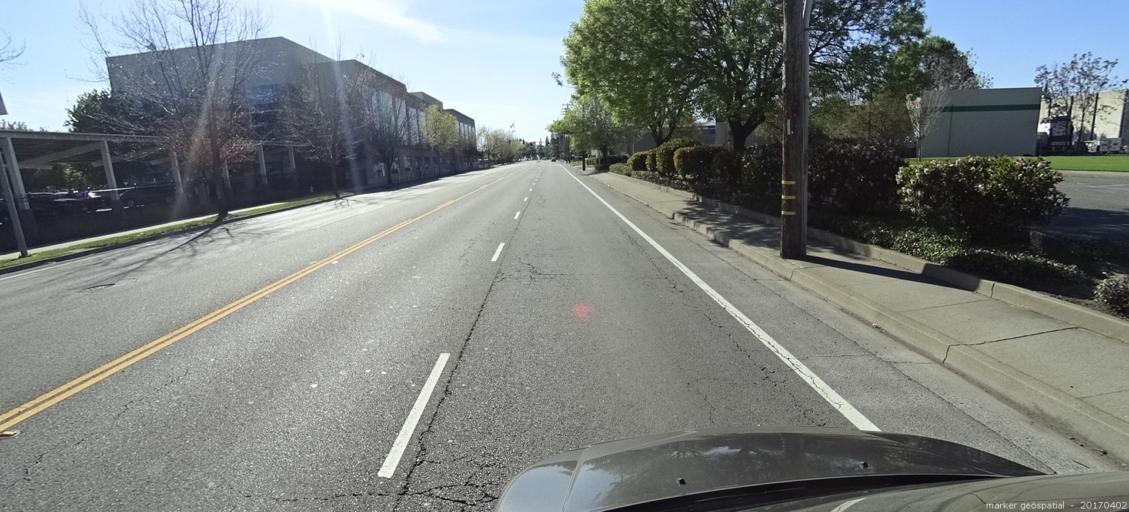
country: US
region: California
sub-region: Sacramento County
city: Sacramento
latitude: 38.5973
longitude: -121.4979
